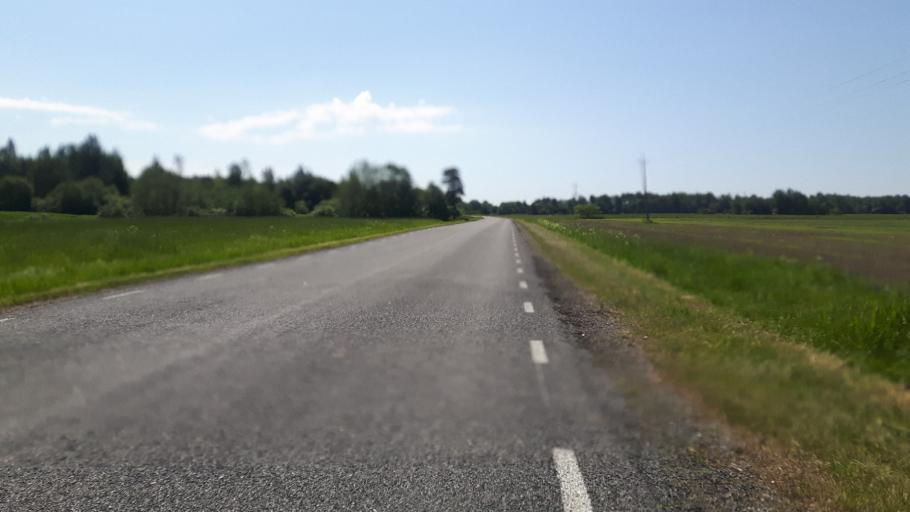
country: EE
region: Paernumaa
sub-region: Vaendra vald (alev)
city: Vandra
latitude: 58.6076
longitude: 25.0215
